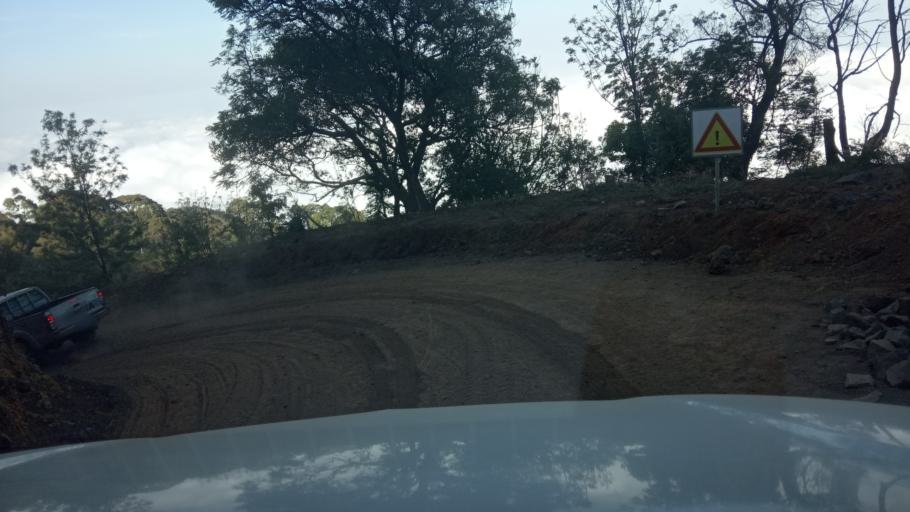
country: CV
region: Mosteiros
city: Porto dos Mosteiros
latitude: 14.9981
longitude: -24.3449
